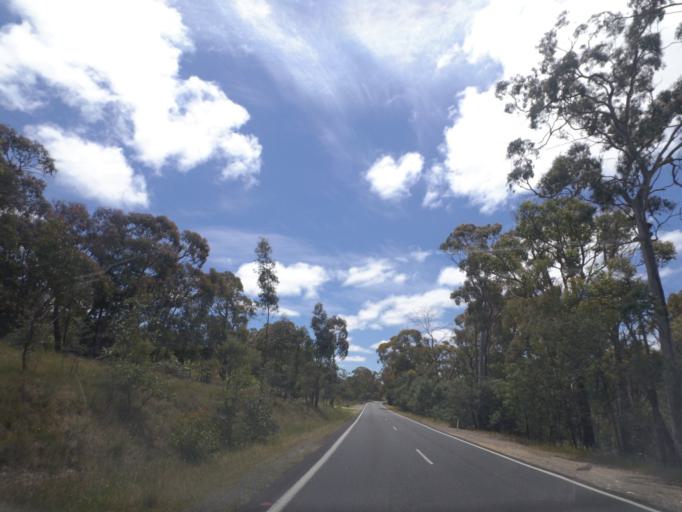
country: AU
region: Victoria
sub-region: Mount Alexander
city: Castlemaine
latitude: -37.3025
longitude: 144.1632
